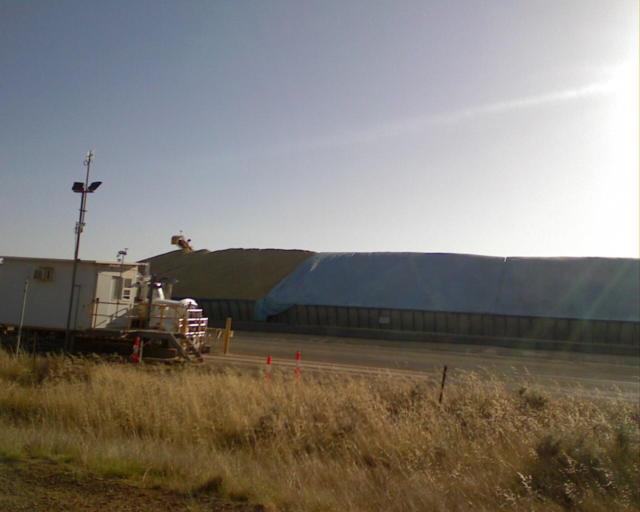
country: AU
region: Western Australia
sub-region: Wongan-Ballidu
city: Wongan Hills
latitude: -30.3575
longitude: 117.1134
